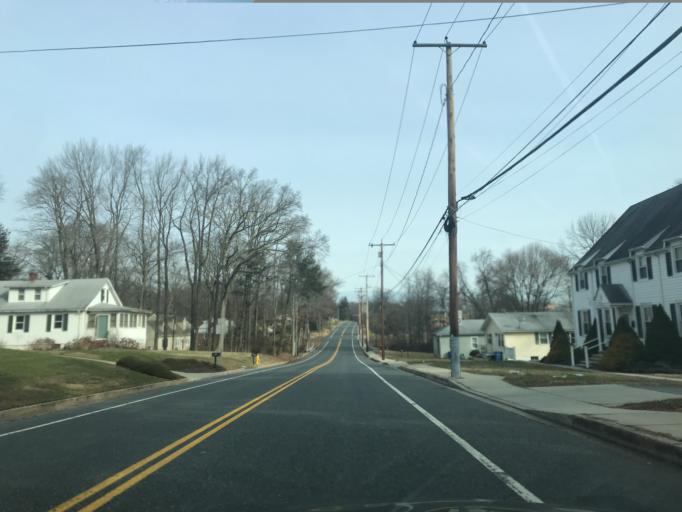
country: US
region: Maryland
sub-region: Harford County
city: Aberdeen
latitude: 39.5138
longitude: -76.1746
